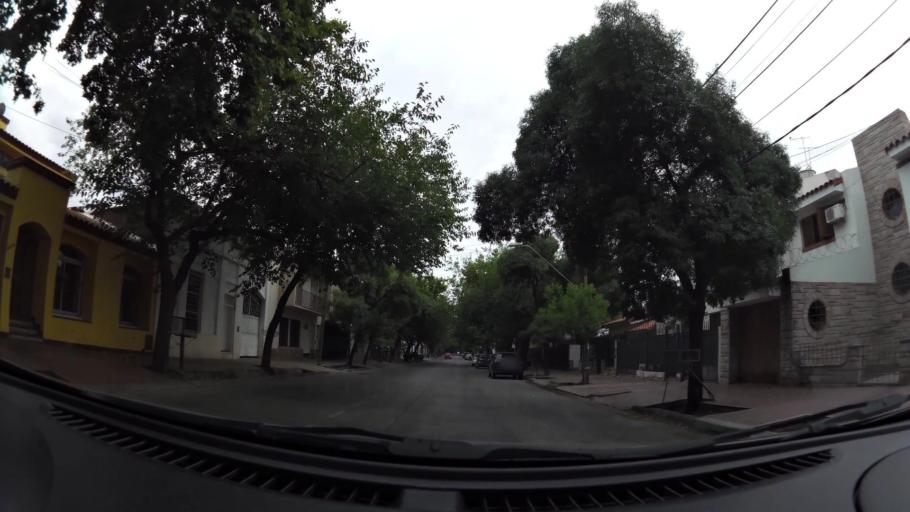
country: AR
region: Mendoza
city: Mendoza
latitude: -32.8861
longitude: -68.8611
